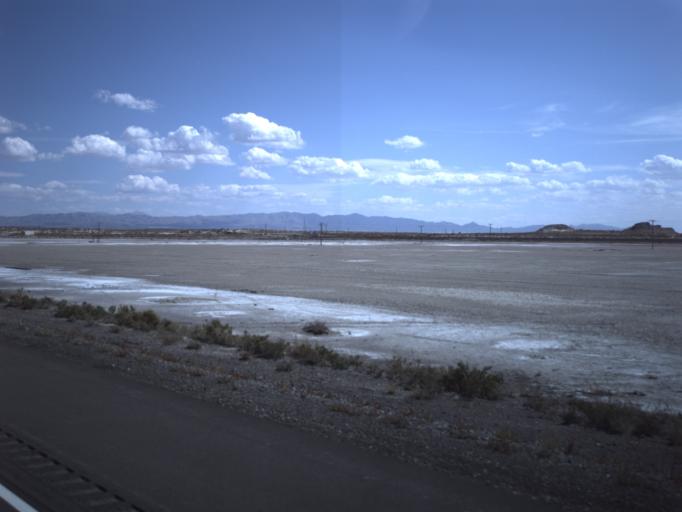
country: US
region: Utah
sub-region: Tooele County
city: Wendover
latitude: 40.7270
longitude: -113.2939
